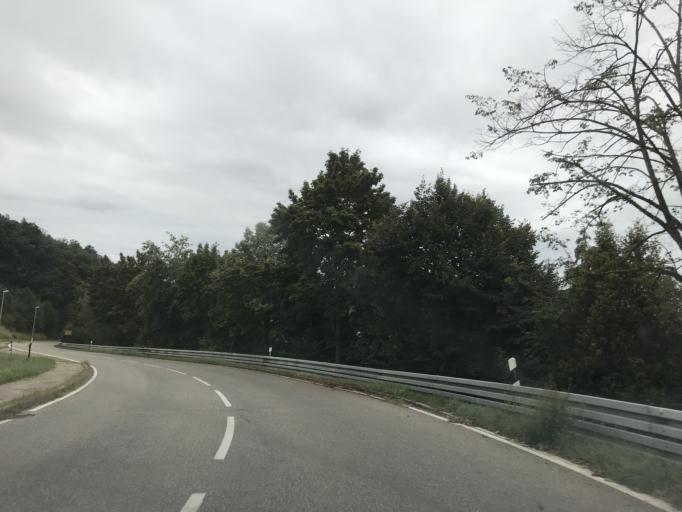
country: DE
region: Baden-Wuerttemberg
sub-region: Freiburg Region
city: Murg
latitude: 47.5720
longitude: 8.0352
